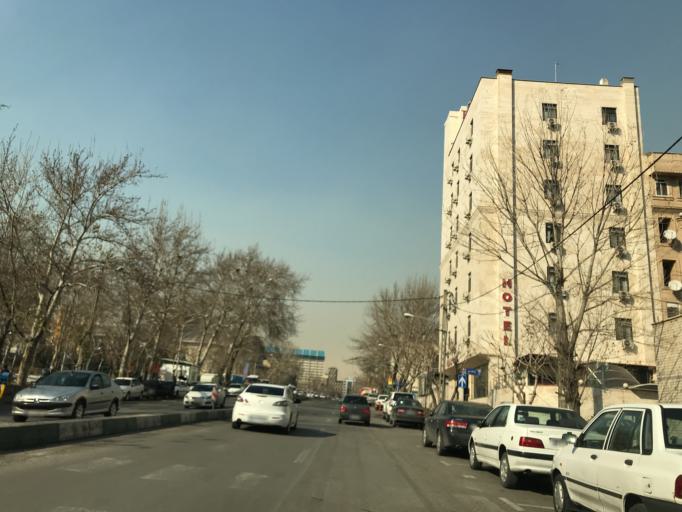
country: IR
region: Tehran
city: Tehran
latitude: 35.7103
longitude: 51.3966
